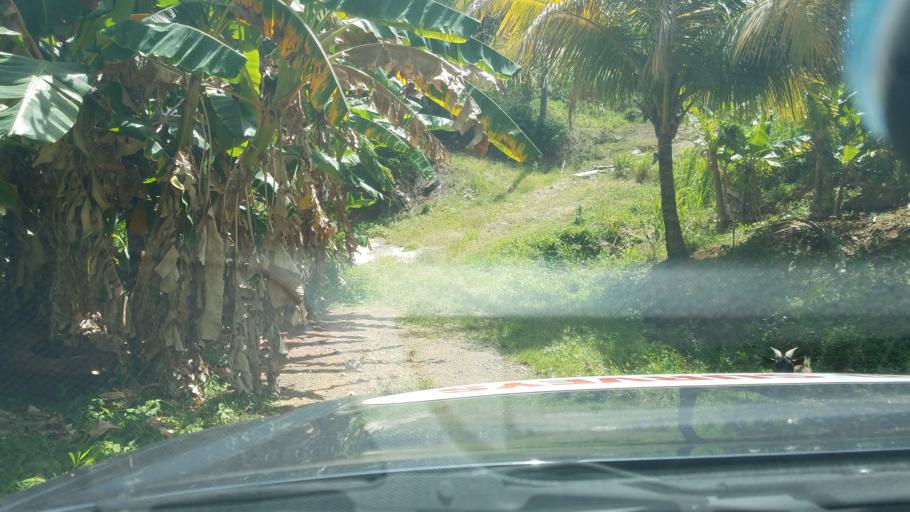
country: LC
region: Castries Quarter
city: Bisee
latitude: 14.0318
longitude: -60.9573
